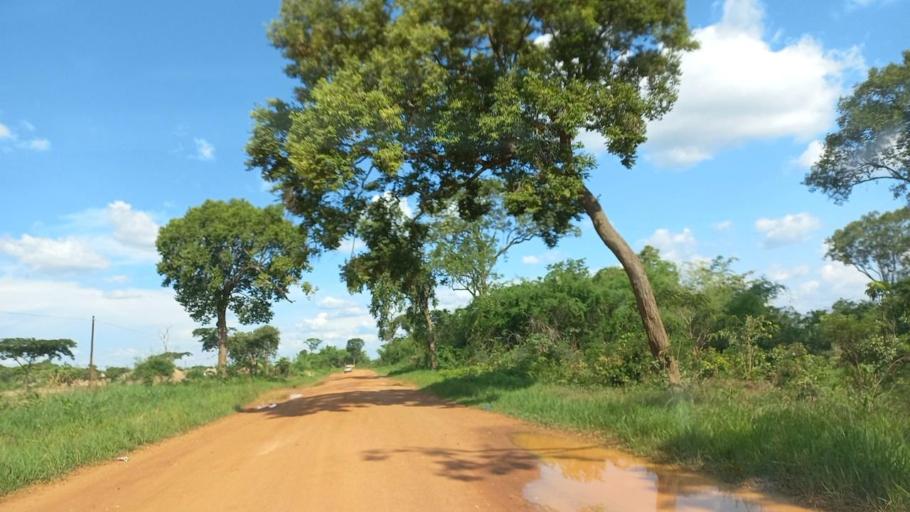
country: ZM
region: Copperbelt
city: Kitwe
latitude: -12.8638
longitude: 28.3783
